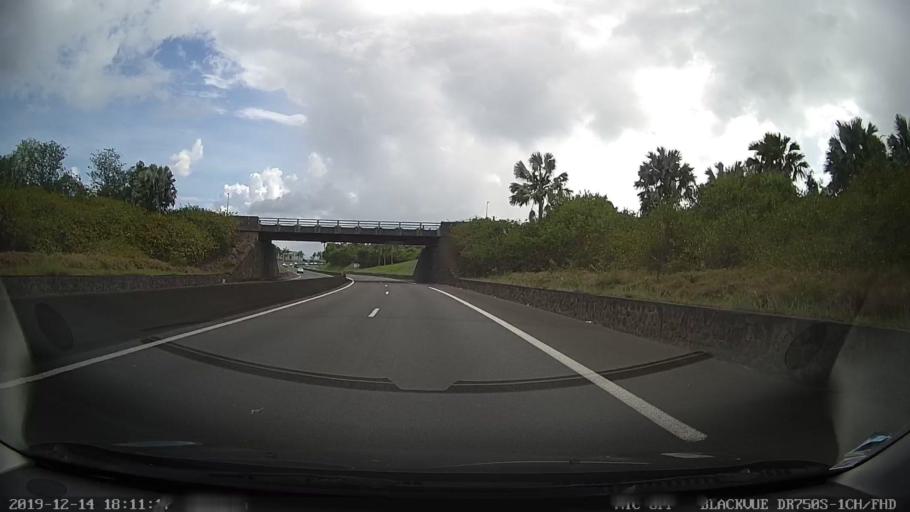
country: RE
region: Reunion
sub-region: Reunion
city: Sainte-Marie
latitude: -20.9016
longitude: 55.5594
